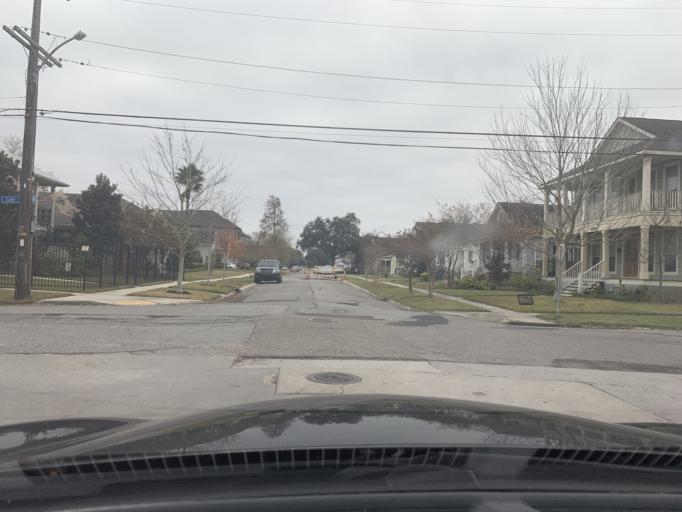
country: US
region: Louisiana
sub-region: Jefferson Parish
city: Metairie
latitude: 30.0091
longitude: -90.1109
